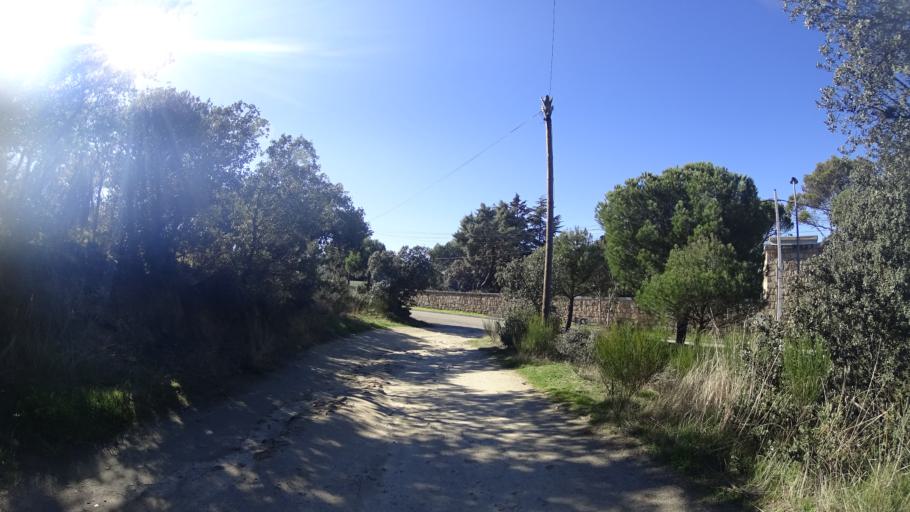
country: ES
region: Madrid
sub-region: Provincia de Madrid
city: Torrelodones
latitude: 40.5925
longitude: -3.9504
